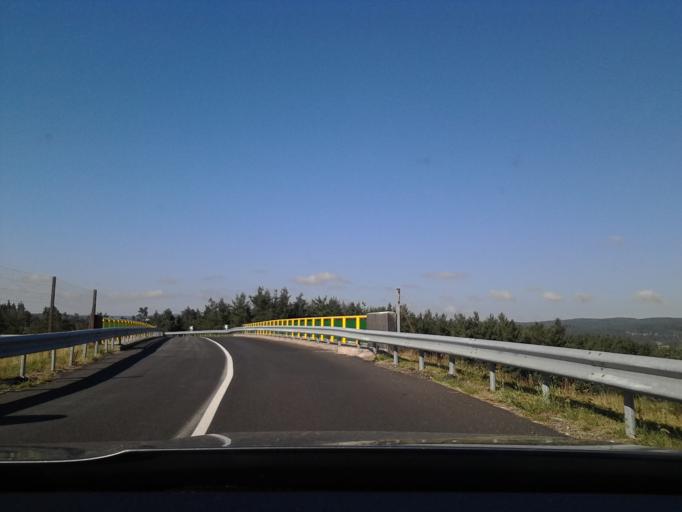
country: FR
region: Languedoc-Roussillon
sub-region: Departement de la Lozere
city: Aumont-Aubrac
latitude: 44.7005
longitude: 3.2823
